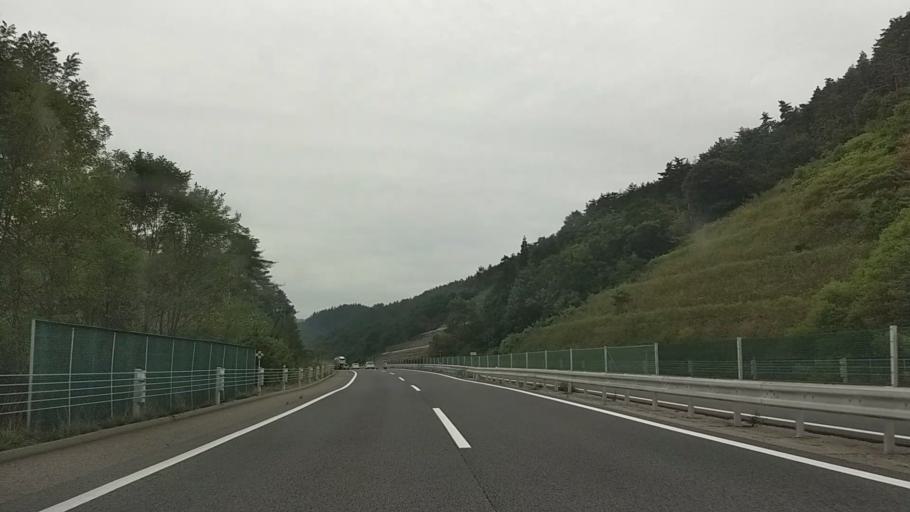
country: JP
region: Nagano
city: Hotaka
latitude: 36.4050
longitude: 138.0008
